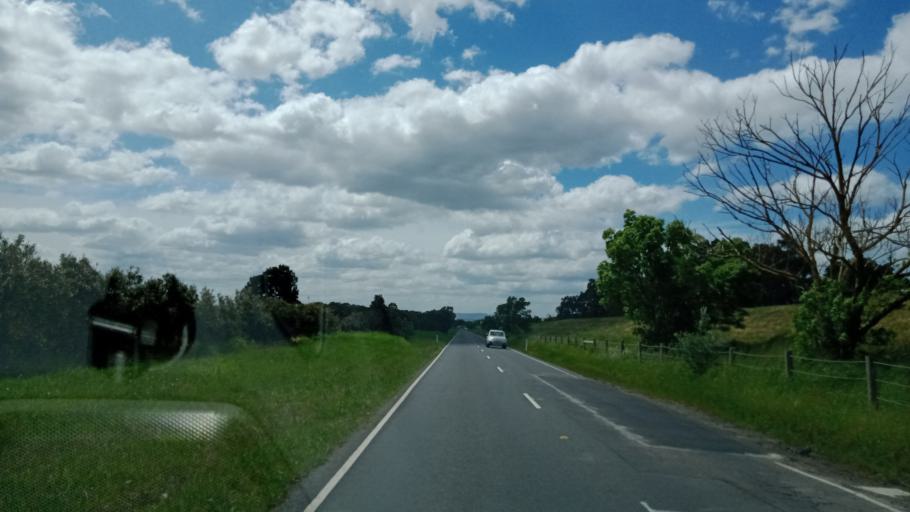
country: AU
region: Victoria
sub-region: Kingston
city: Patterson Lakes
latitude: -38.0417
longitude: 145.1751
